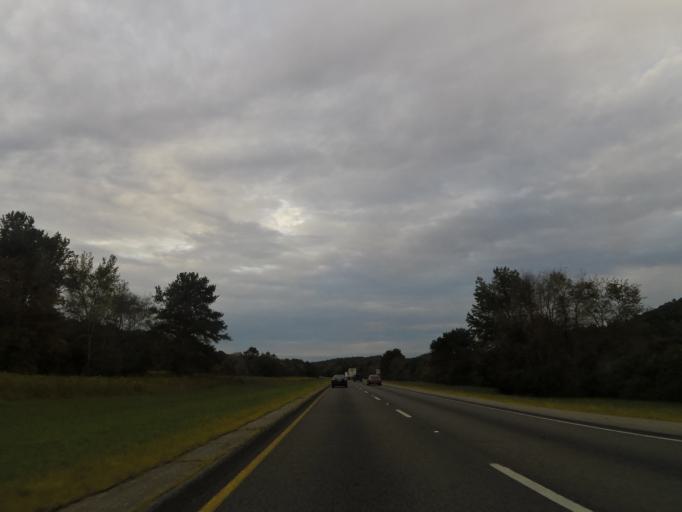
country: US
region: Alabama
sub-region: Jefferson County
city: Argo
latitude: 33.6653
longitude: -86.5593
